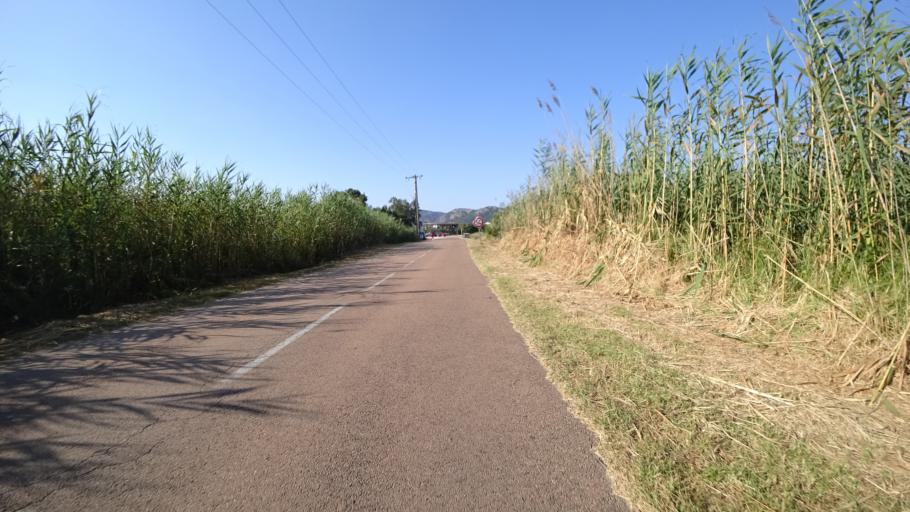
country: FR
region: Corsica
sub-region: Departement de la Corse-du-Sud
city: Porto-Vecchio
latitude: 41.6223
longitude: 9.3338
